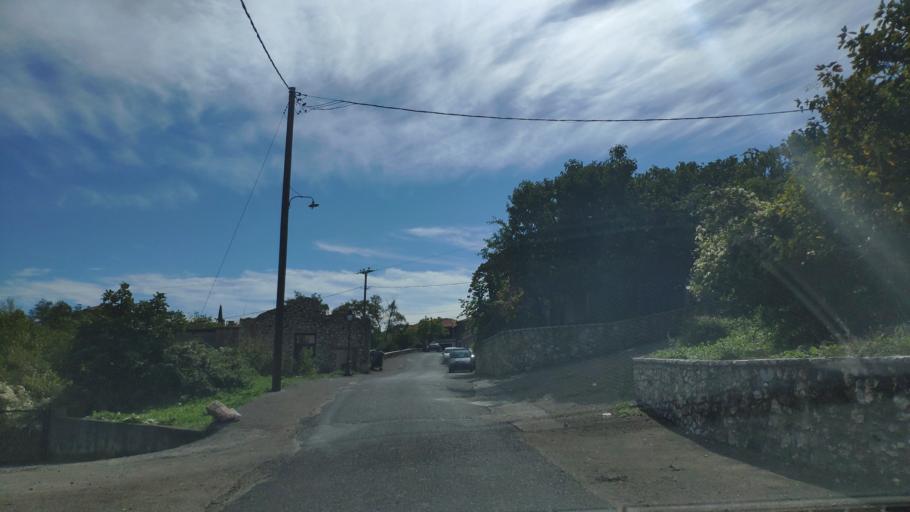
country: GR
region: Peloponnese
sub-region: Nomos Arkadias
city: Dimitsana
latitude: 37.5220
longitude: 22.0718
